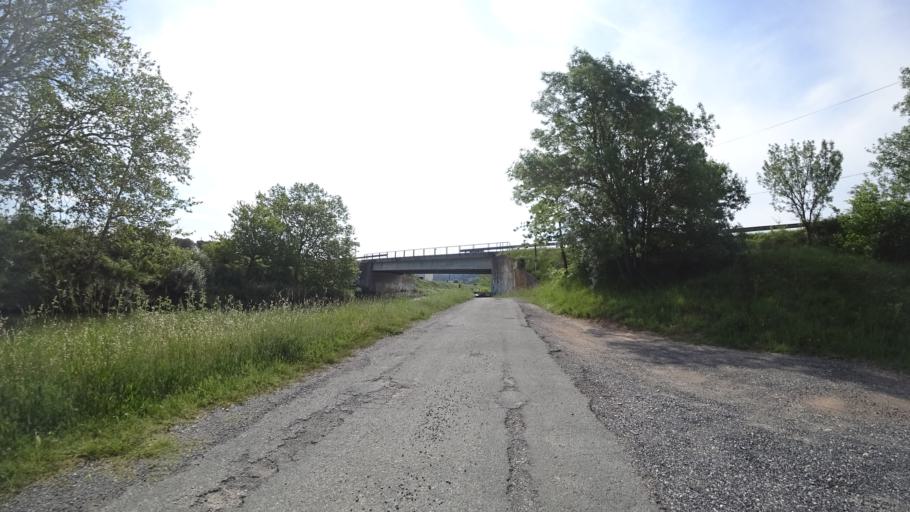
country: FR
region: Languedoc-Roussillon
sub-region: Departement de l'Herault
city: Olonzac
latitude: 43.2666
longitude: 2.7403
